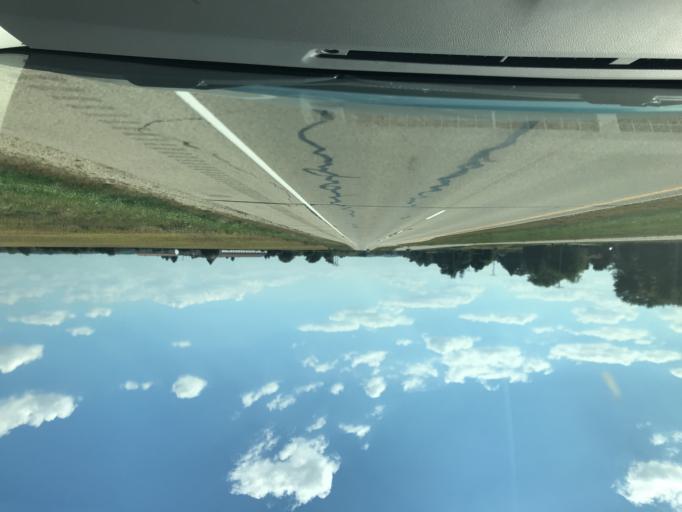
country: US
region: Wisconsin
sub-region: Walworth County
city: Pell Lake
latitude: 42.5968
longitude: -88.3695
